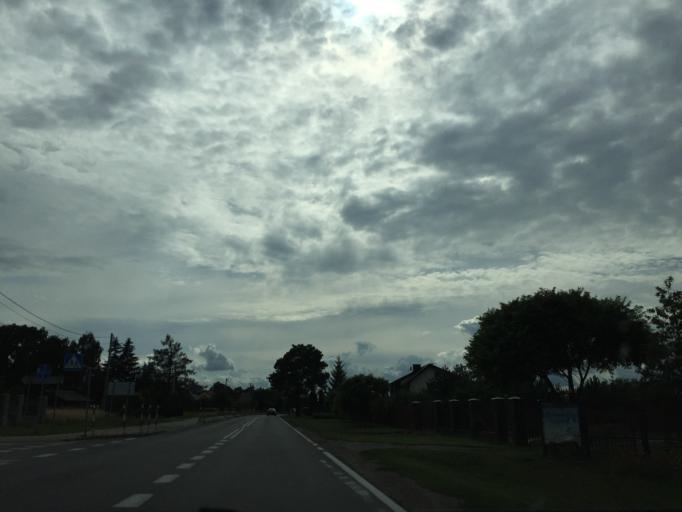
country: PL
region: Lublin Voivodeship
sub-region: Powiat lukowski
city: Lukow
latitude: 51.9478
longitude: 22.4385
